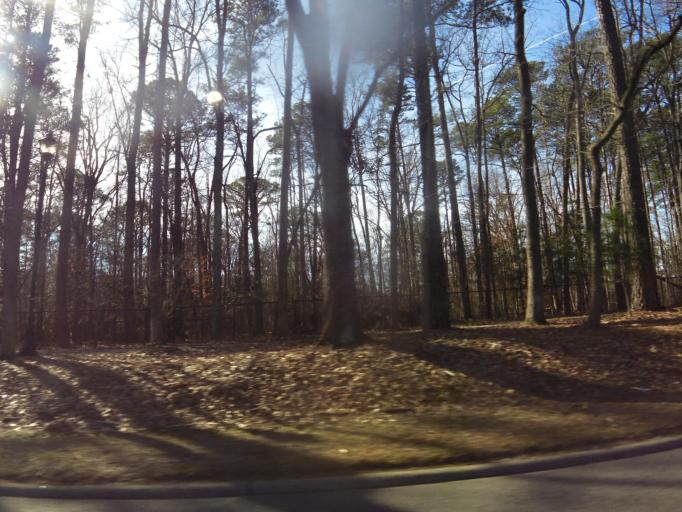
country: US
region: Virginia
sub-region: City of Newport News
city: Newport News
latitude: 37.0544
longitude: -76.4806
